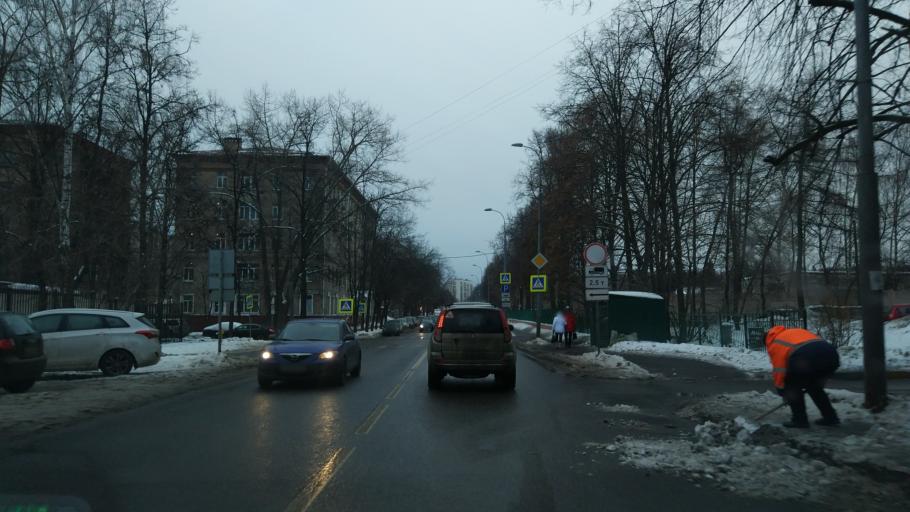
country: RU
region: Moskovskaya
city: Izmaylovo
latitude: 55.7909
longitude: 37.8235
